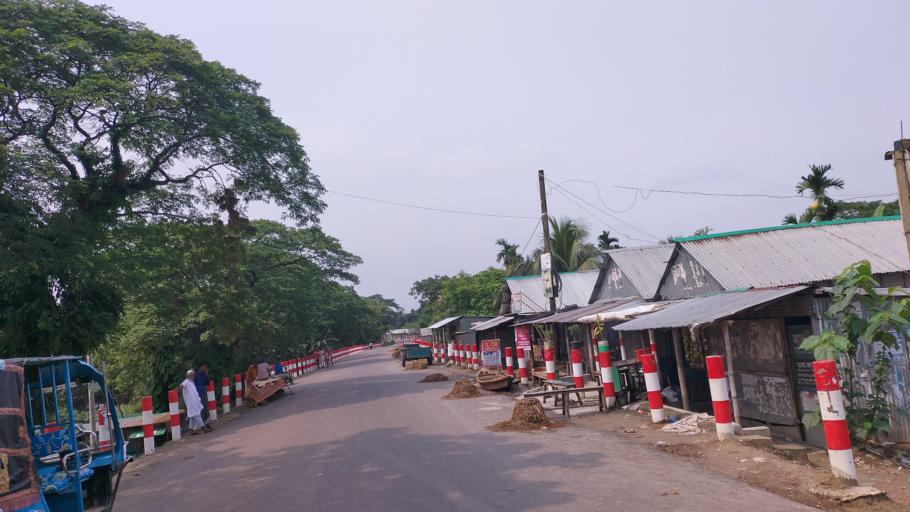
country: BD
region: Dhaka
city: Netrakona
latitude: 24.9553
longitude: 90.8345
